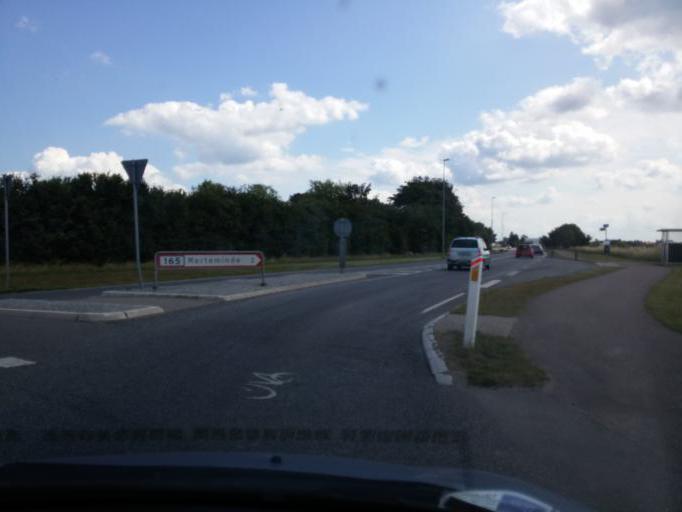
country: DK
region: South Denmark
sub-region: Kerteminde Kommune
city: Kerteminde
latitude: 55.4532
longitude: 10.6286
